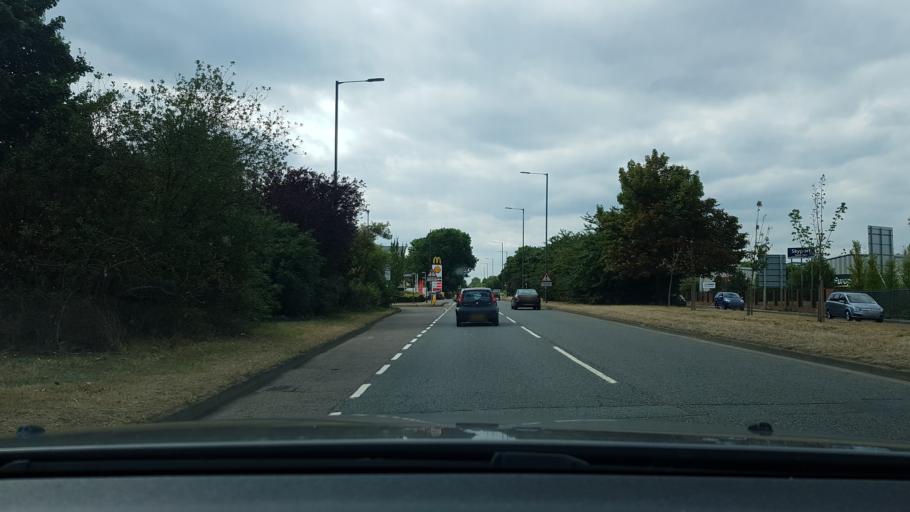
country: GB
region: England
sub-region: Greater London
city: West Drayton
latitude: 51.4818
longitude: -0.4782
